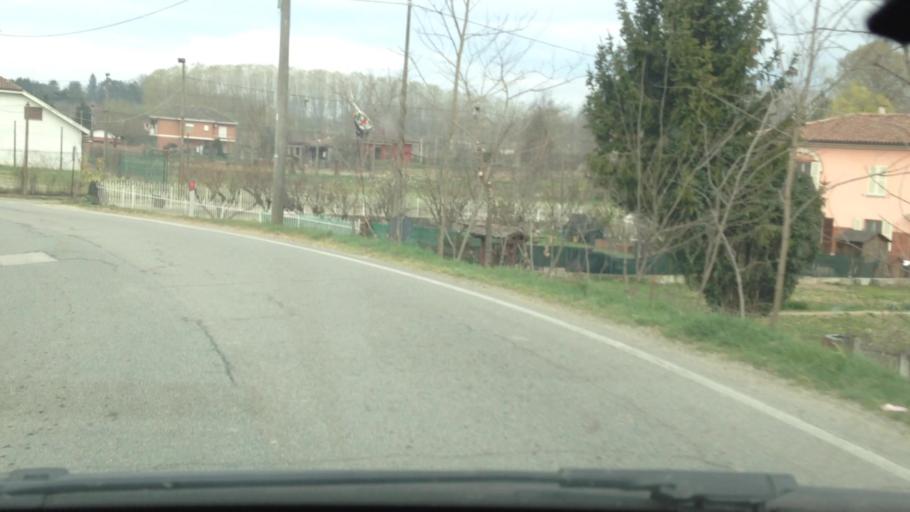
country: IT
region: Piedmont
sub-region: Provincia di Asti
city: Revigliasco d'Asti
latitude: 44.8902
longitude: 8.1472
